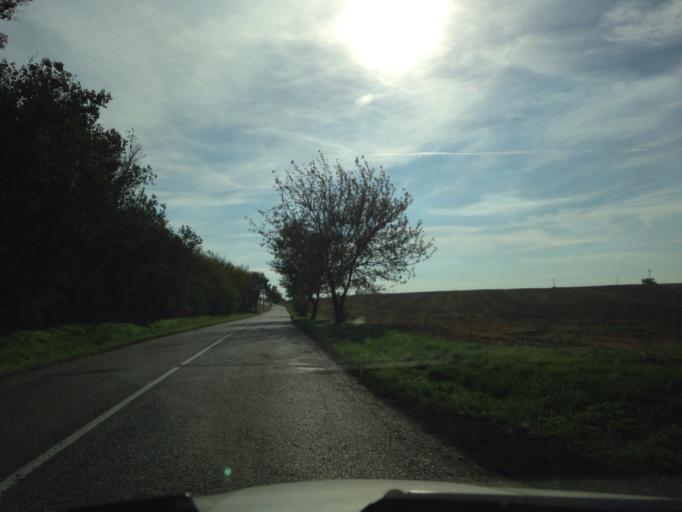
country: SK
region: Nitriansky
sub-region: Okres Komarno
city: Hurbanovo
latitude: 47.8751
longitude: 18.2850
